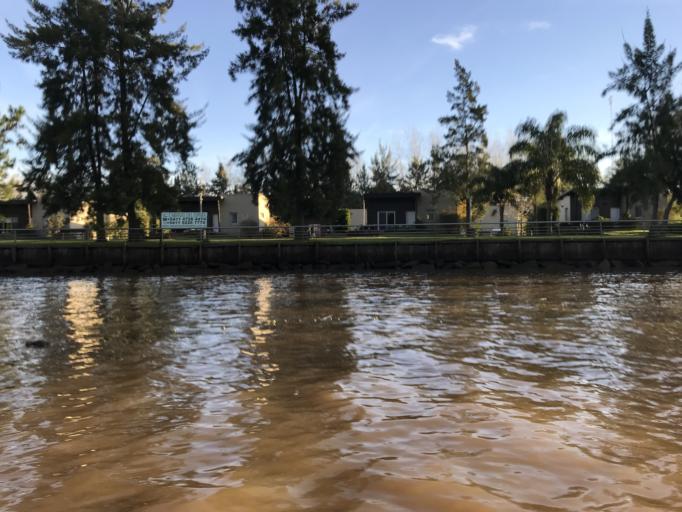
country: AR
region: Buenos Aires
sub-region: Partido de Tigre
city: Tigre
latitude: -34.3753
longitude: -58.5785
